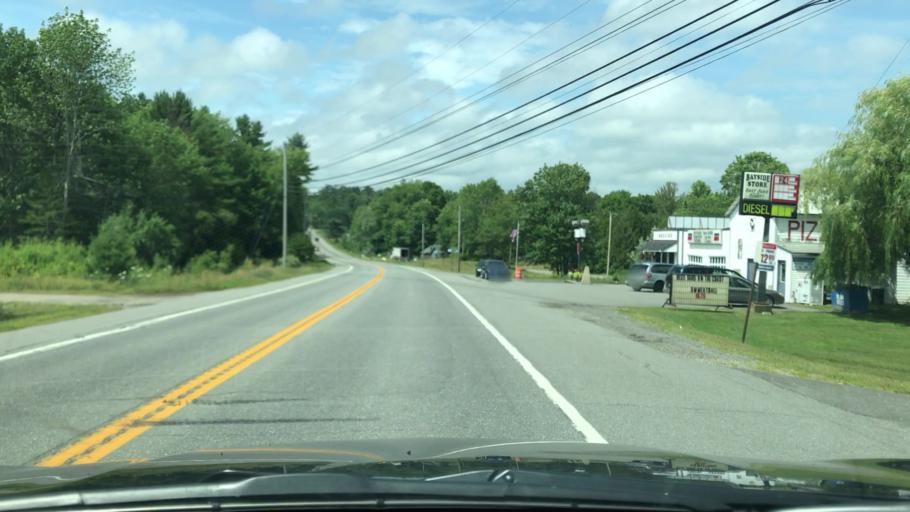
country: US
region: Maine
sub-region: Waldo County
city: Belfast
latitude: 44.3824
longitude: -68.9859
